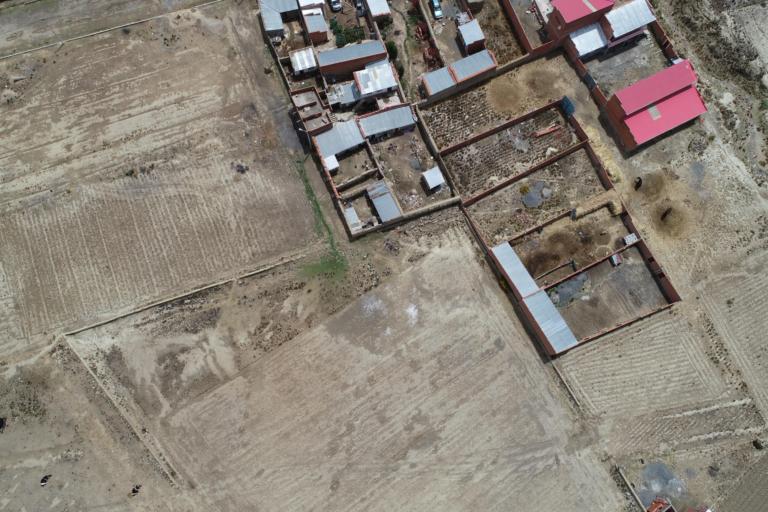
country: BO
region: La Paz
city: Achacachi
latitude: -16.0539
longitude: -68.6789
